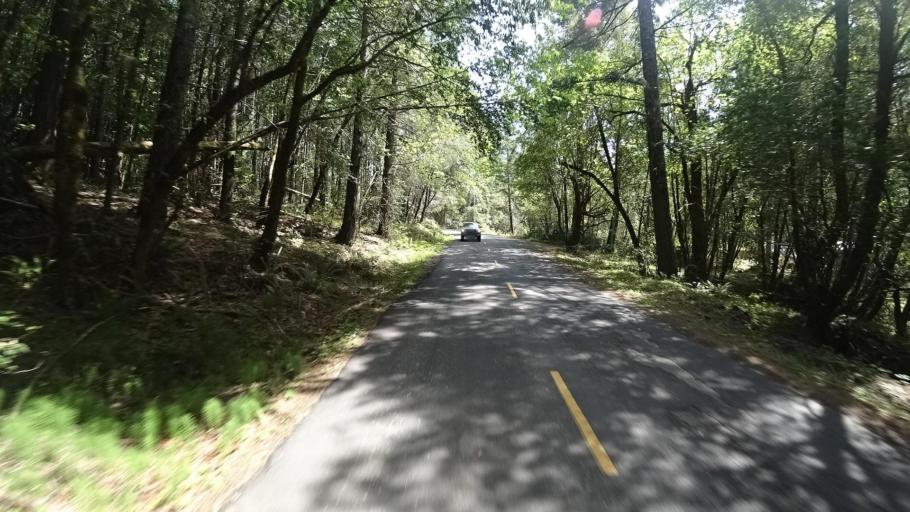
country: US
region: California
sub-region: Humboldt County
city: Redway
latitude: 40.3588
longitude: -123.7240
